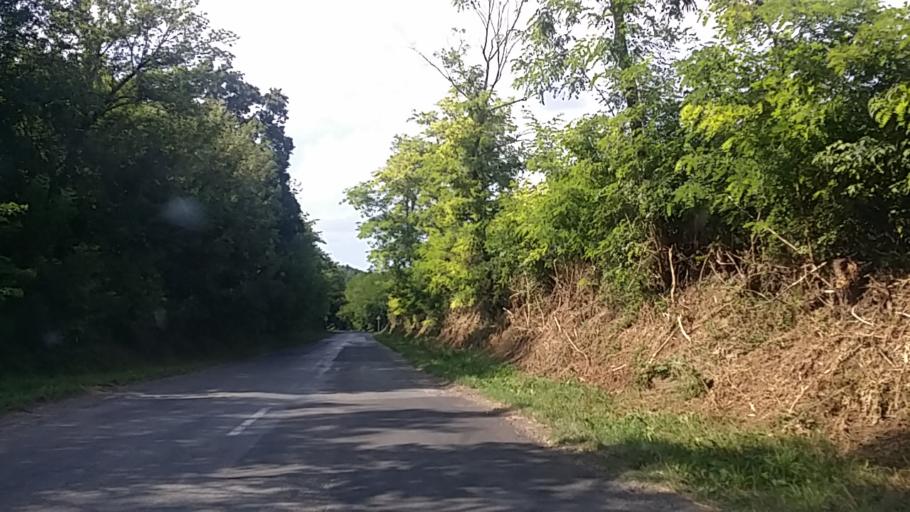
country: HU
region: Tolna
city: Gyonk
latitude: 46.5452
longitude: 18.4826
